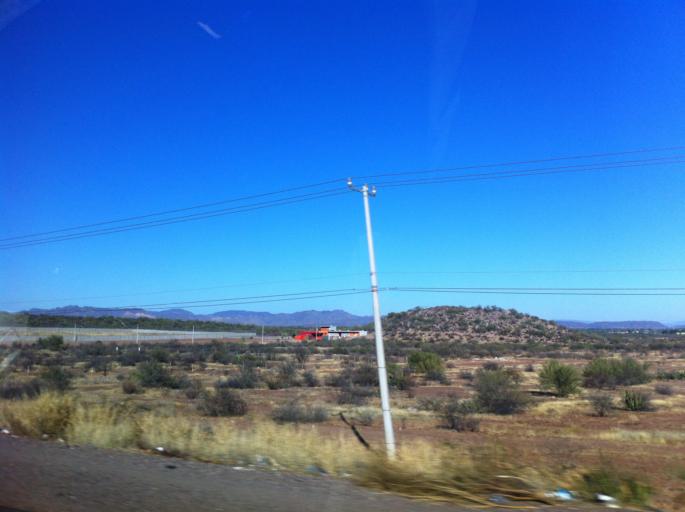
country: MX
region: Sonora
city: Heroica Guaymas
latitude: 27.9686
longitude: -110.9368
